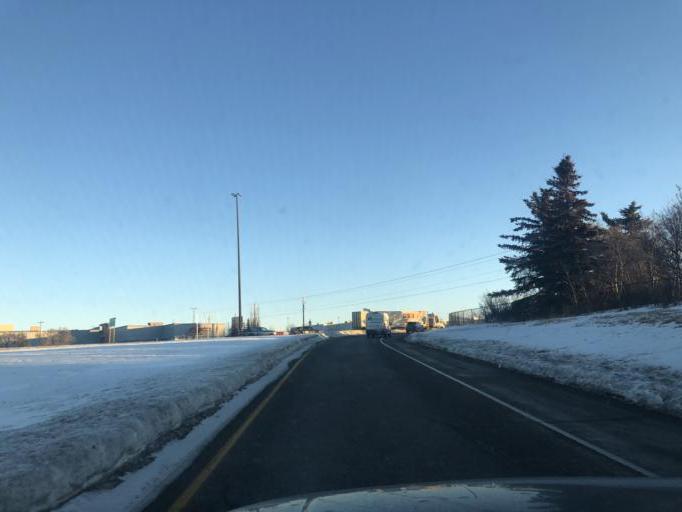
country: CA
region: Alberta
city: Calgary
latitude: 51.0952
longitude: -114.0378
